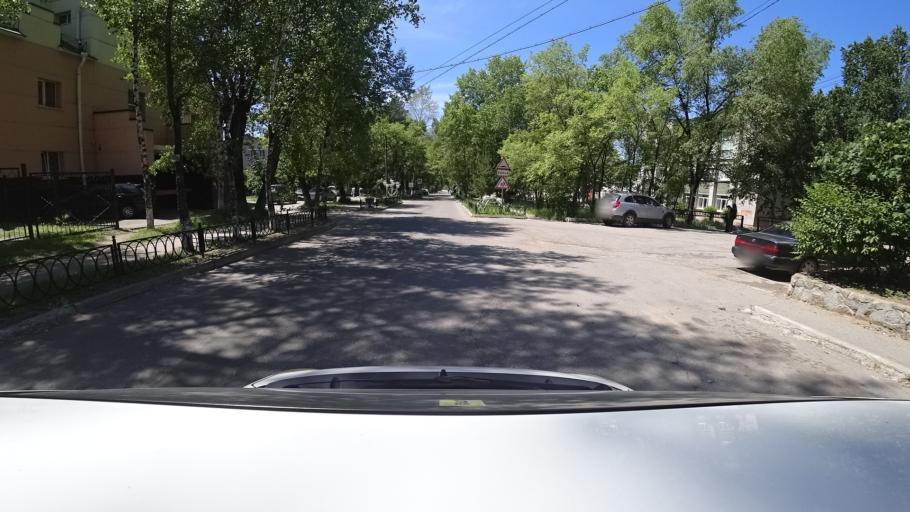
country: RU
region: Khabarovsk Krai
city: Topolevo
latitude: 48.5069
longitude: 135.1733
